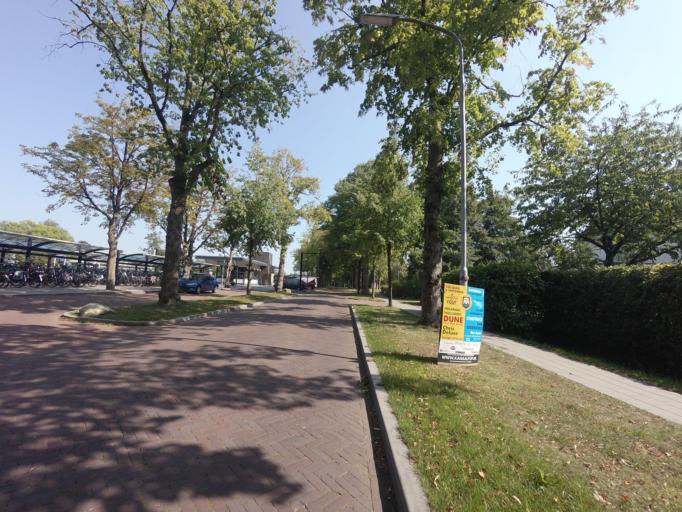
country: NL
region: Groningen
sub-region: Gemeente Zuidhorn
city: Zuidhorn
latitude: 53.2483
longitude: 6.4055
